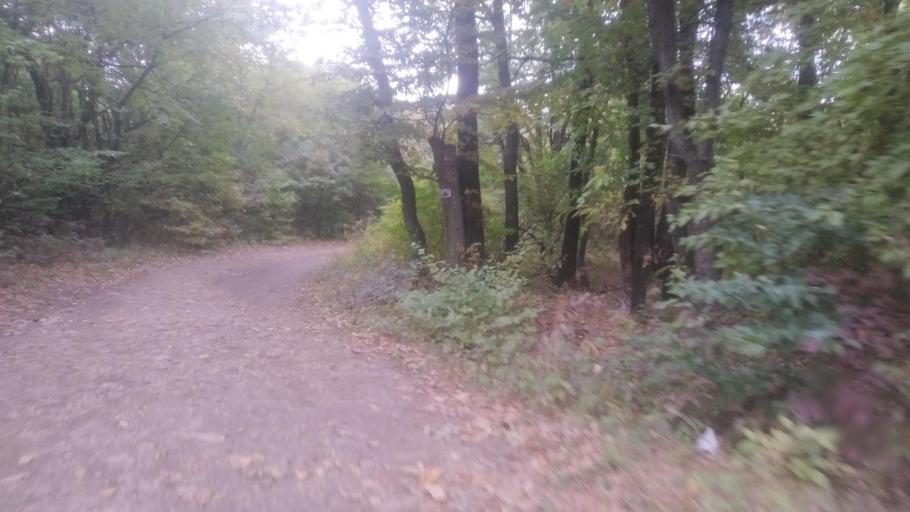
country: HU
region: Pest
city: Telki
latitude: 47.5505
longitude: 18.8663
